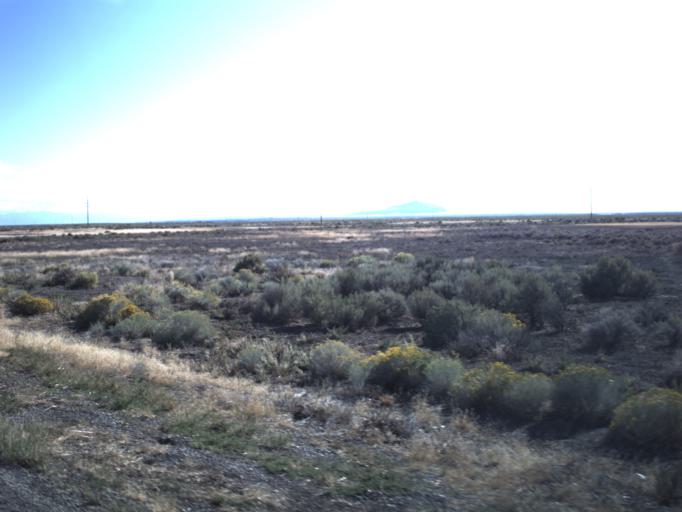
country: US
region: Utah
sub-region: Millard County
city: Delta
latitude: 39.3003
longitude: -112.4716
